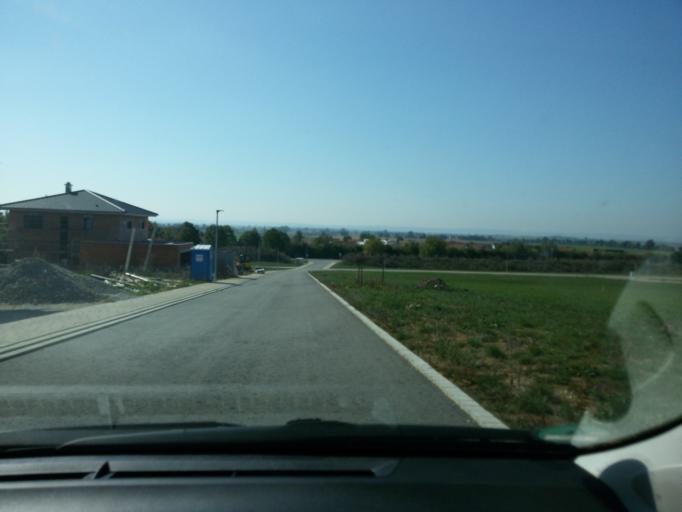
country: DE
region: Bavaria
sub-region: Swabia
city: Oettingen in Bayern
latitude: 48.9599
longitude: 10.5933
